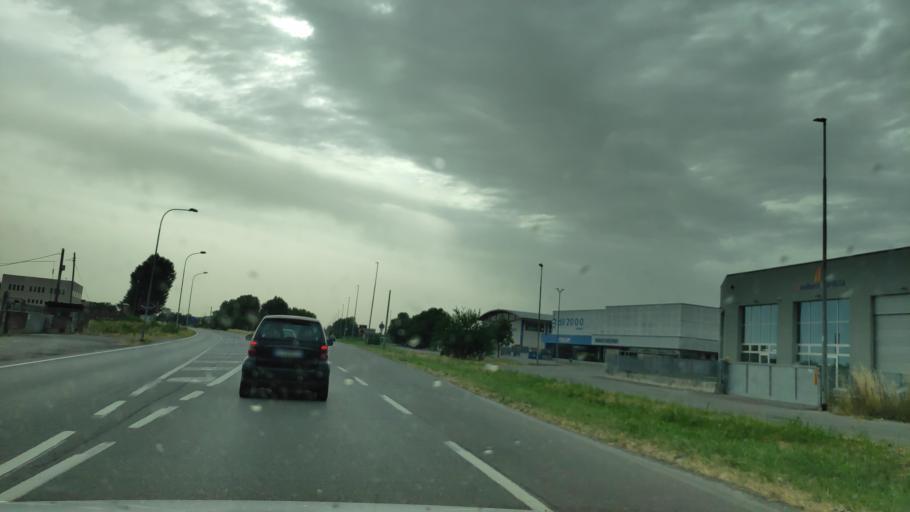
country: IT
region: Lombardy
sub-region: Provincia di Cremona
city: Offanengo
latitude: 45.3775
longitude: 9.7616
